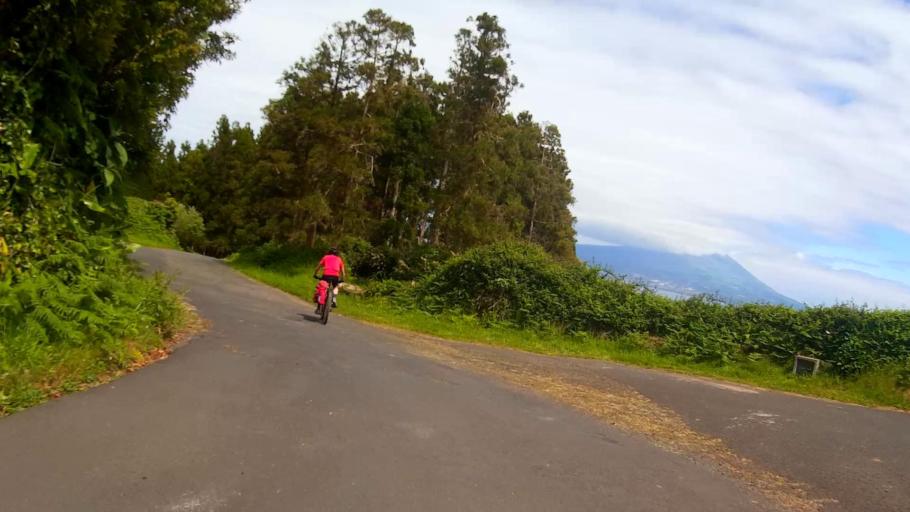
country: PT
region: Azores
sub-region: Horta
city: Horta
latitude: 38.5515
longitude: -28.6682
